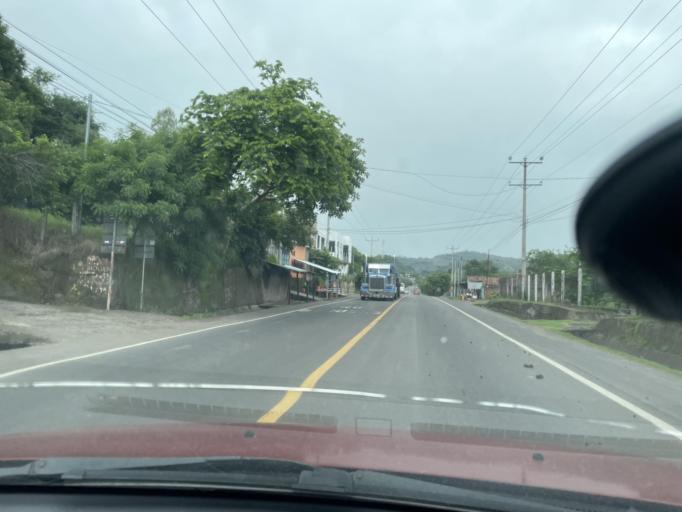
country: SV
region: San Miguel
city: San Miguel
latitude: 13.5119
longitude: -88.1493
